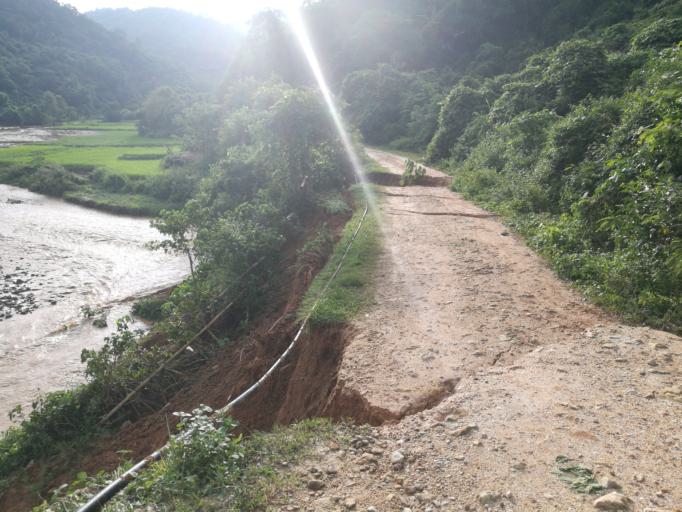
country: LA
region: Phongsali
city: Khoa
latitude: 21.2187
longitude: 102.6801
